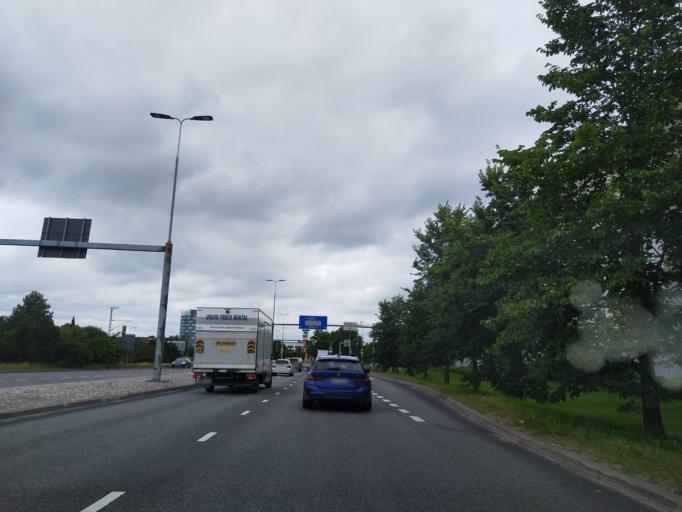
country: FI
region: Varsinais-Suomi
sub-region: Turku
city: Turku
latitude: 60.4566
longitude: 22.2911
